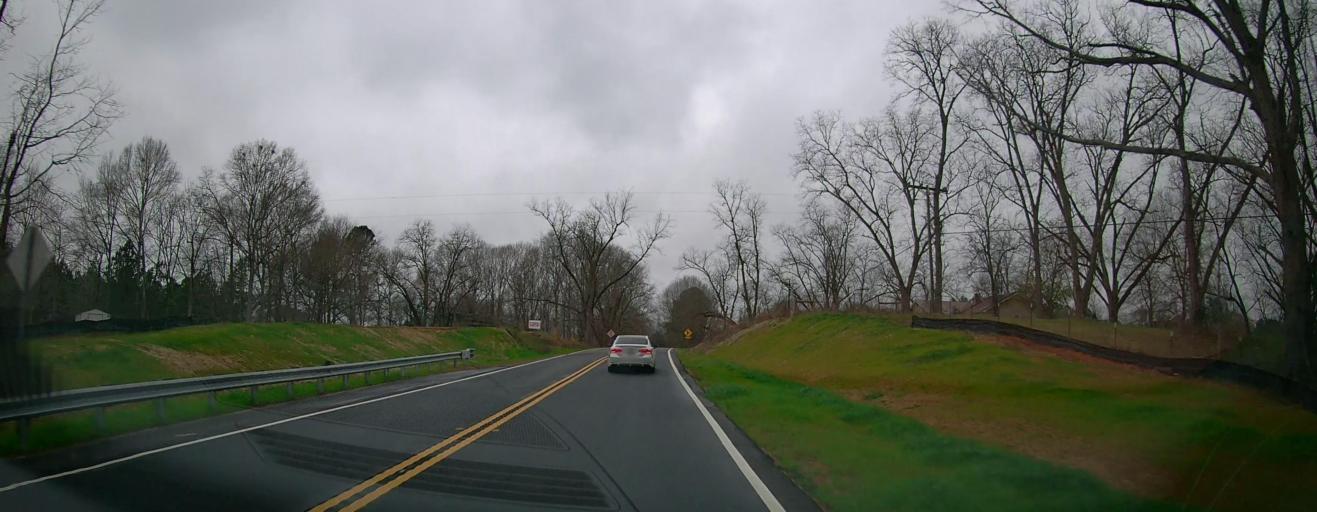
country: US
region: Georgia
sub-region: Pike County
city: Zebulon
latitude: 33.0565
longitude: -84.2852
